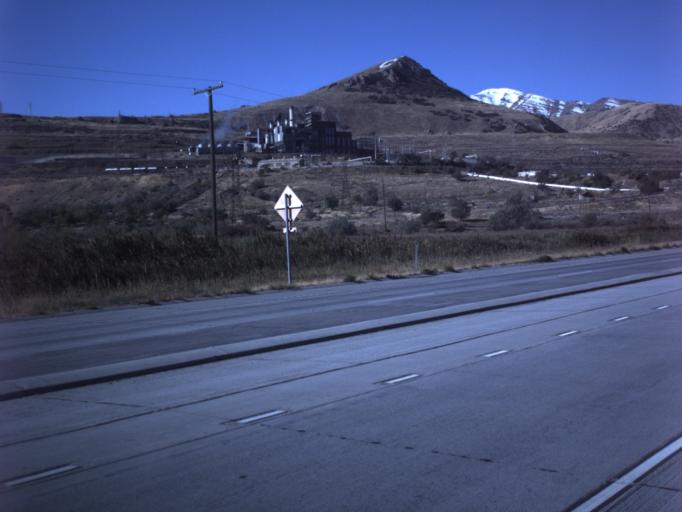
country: US
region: Utah
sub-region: Salt Lake County
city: Magna
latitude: 40.7182
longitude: -112.1122
